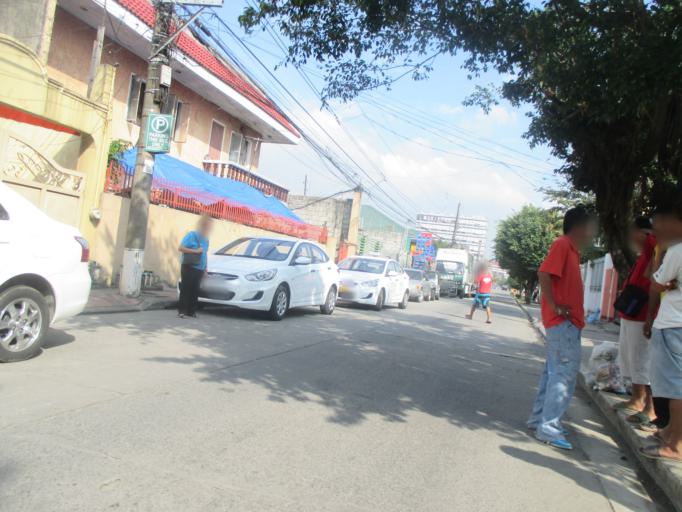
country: PH
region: Metro Manila
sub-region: Marikina
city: Calumpang
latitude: 14.6313
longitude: 121.0997
